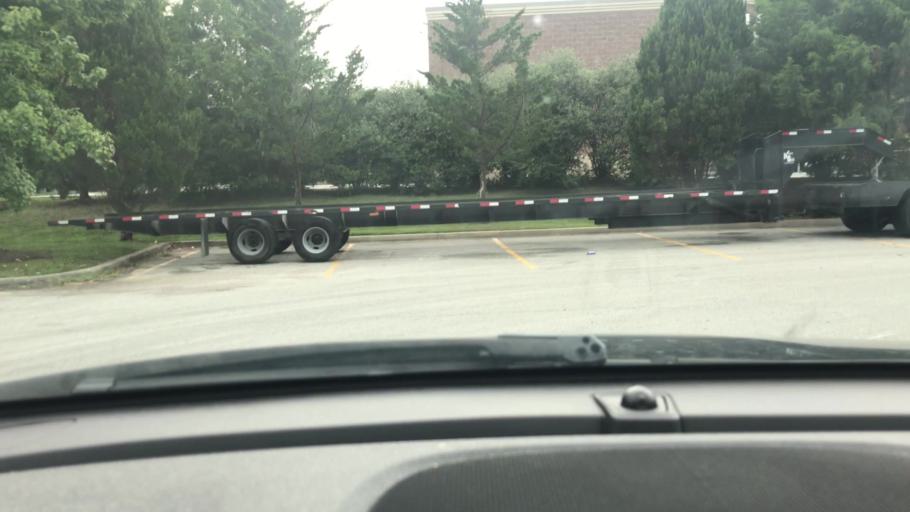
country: US
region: Tennessee
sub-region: Cheatham County
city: Ashland City
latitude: 36.2482
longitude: -87.0347
